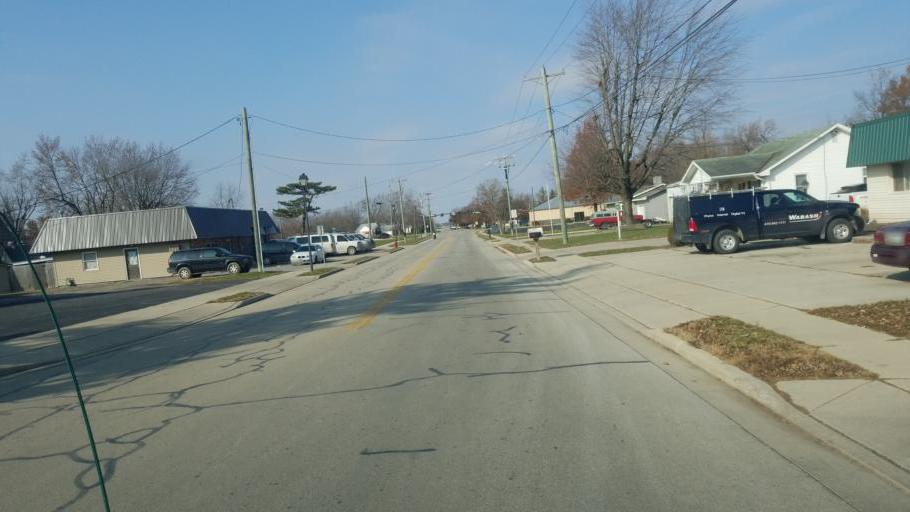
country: US
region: Ohio
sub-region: Mercer County
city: Celina
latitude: 40.5587
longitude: -84.5789
